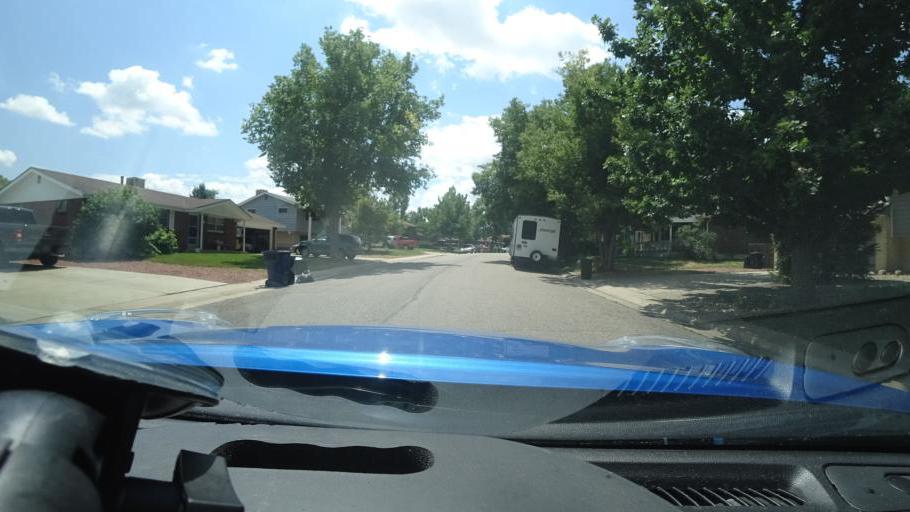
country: US
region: Colorado
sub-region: Adams County
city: Aurora
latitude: 39.7097
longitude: -104.8379
